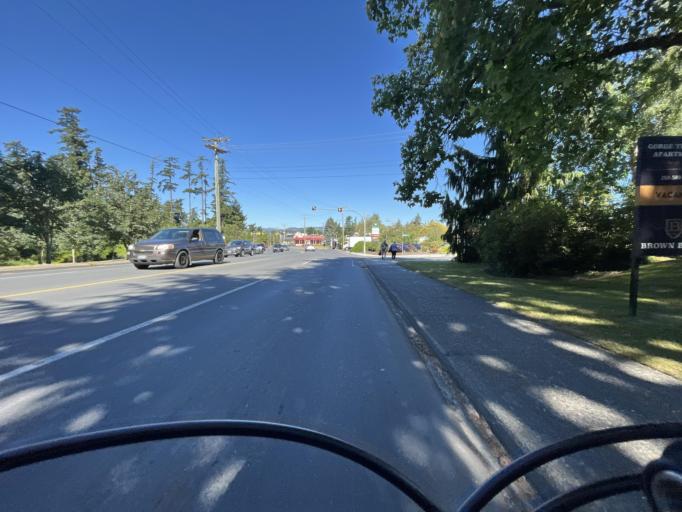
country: CA
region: British Columbia
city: Victoria
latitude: 48.4476
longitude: -123.3983
